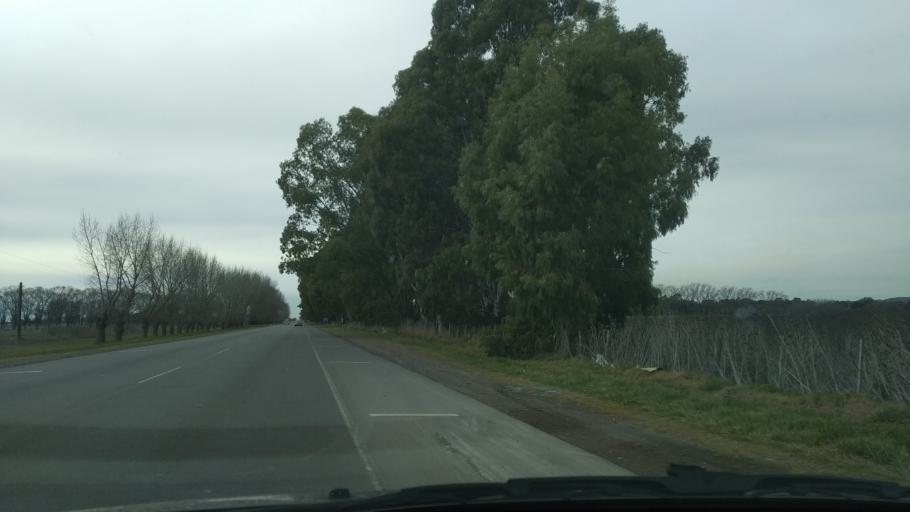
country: AR
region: Buenos Aires
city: Olavarria
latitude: -36.9706
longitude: -60.2730
